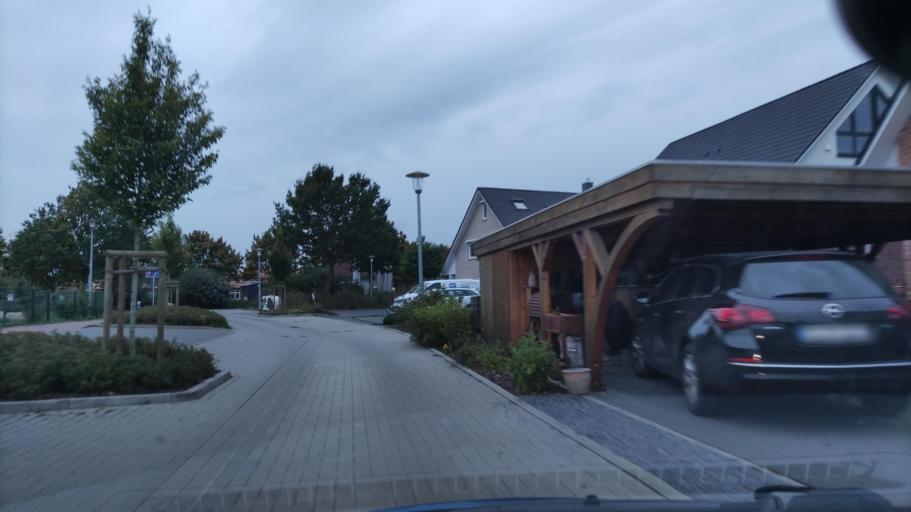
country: DE
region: Schleswig-Holstein
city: Escheburg
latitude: 53.4727
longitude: 10.3127
